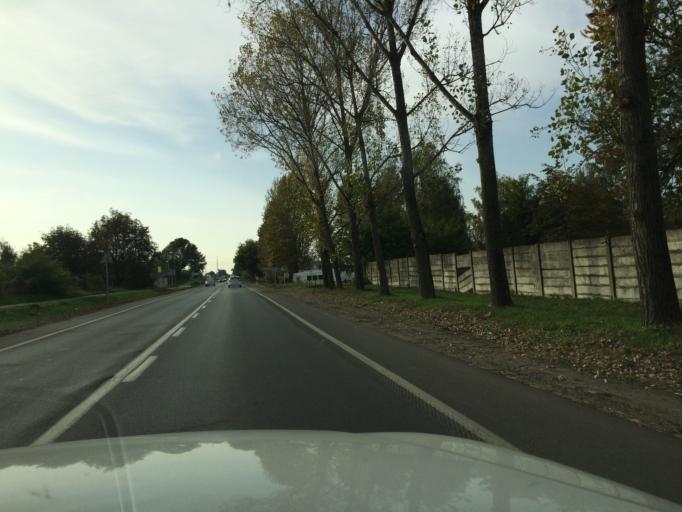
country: HU
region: Szabolcs-Szatmar-Bereg
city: Nyiregyhaza
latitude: 47.9569
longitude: 21.6767
